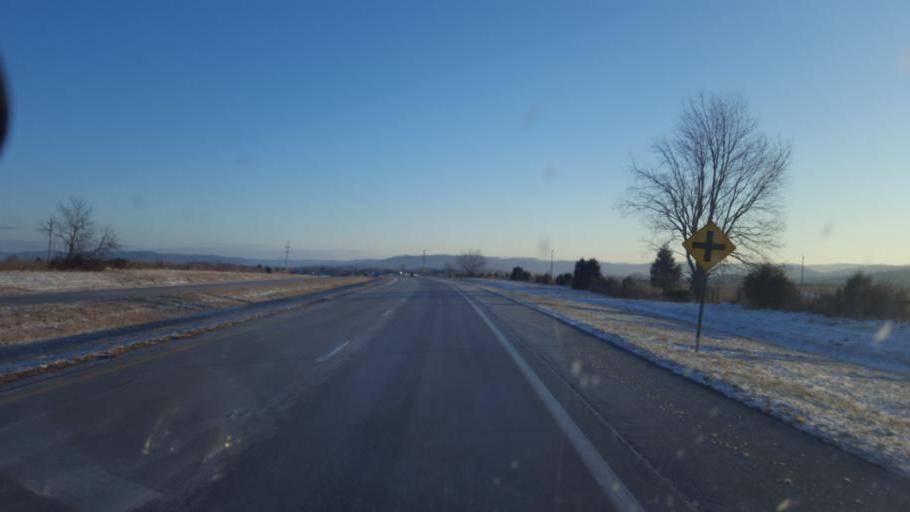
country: US
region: Ohio
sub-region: Adams County
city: Peebles
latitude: 38.9532
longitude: -83.3677
